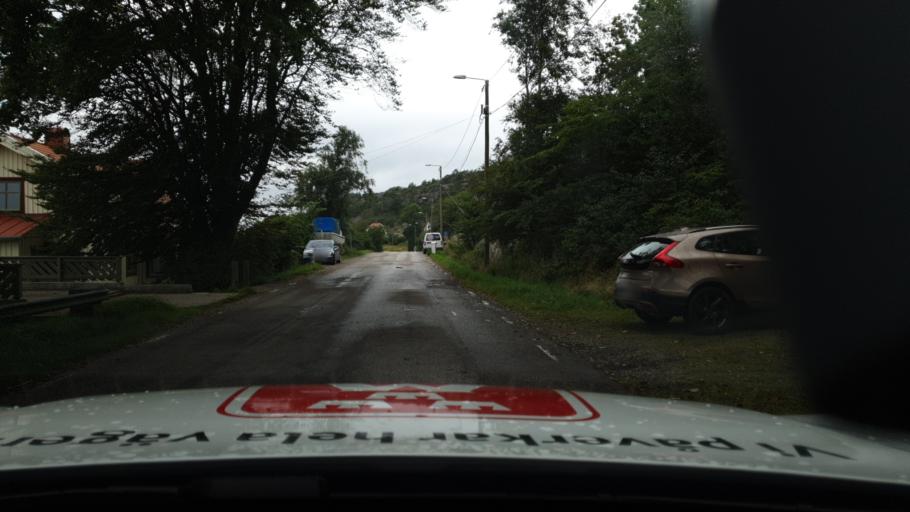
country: SE
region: Vaestra Goetaland
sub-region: Kungalvs Kommun
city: Kode
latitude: 57.8987
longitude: 11.7263
